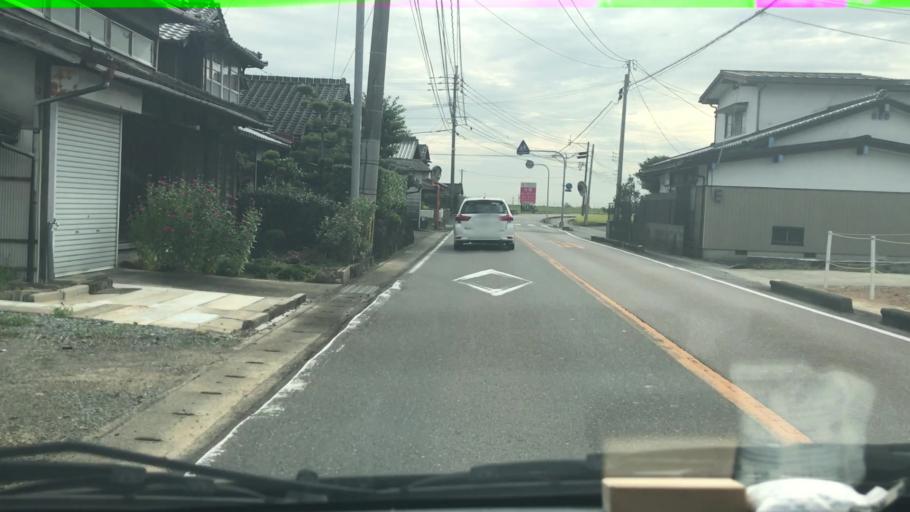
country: JP
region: Saga Prefecture
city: Takeocho-takeo
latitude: 33.2053
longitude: 130.0903
